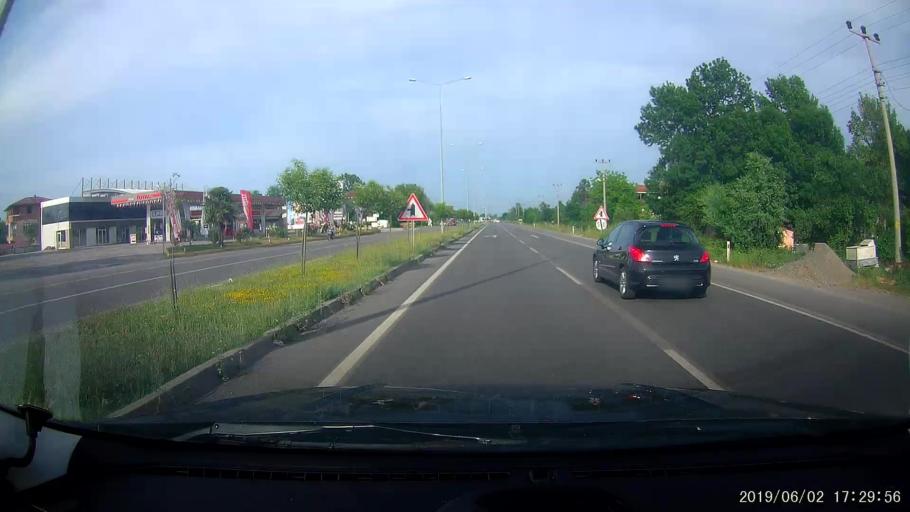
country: TR
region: Samsun
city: Carsamba
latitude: 41.2137
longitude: 36.7696
